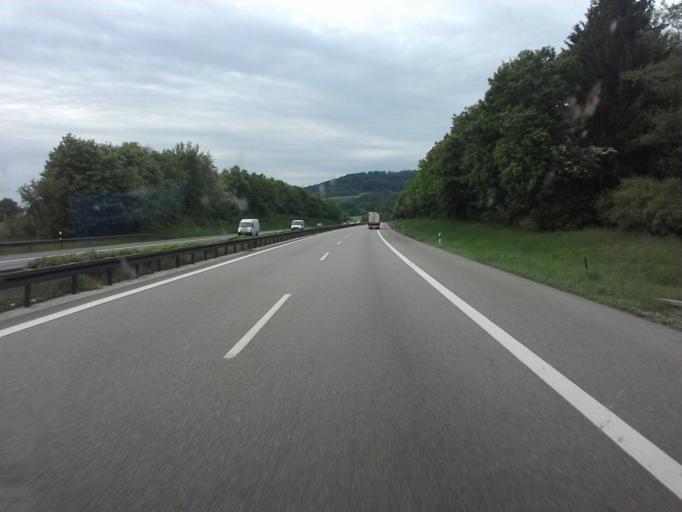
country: DE
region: Bavaria
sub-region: Upper Palatinate
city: Pilsach
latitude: 49.3315
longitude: 11.4548
